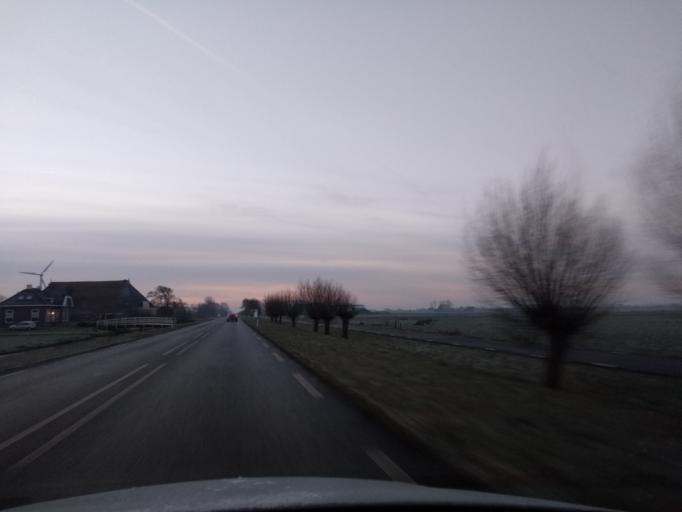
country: NL
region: Friesland
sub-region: Sudwest Fryslan
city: Woudsend
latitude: 52.9585
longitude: 5.6522
